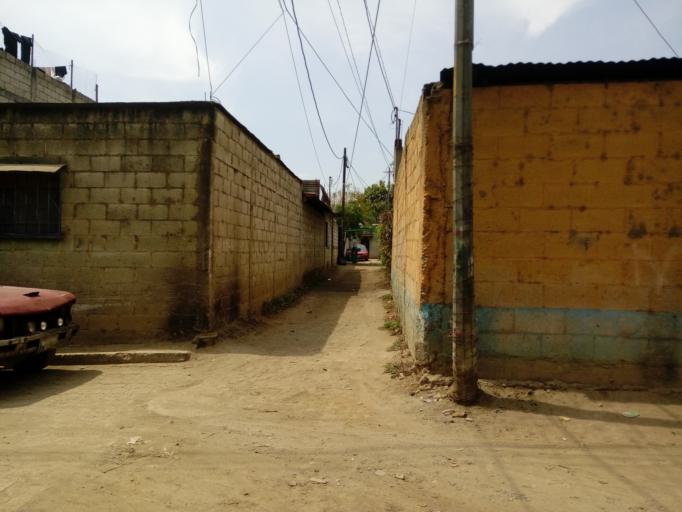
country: GT
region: Guatemala
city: Amatitlan
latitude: 14.4927
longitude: -90.6203
